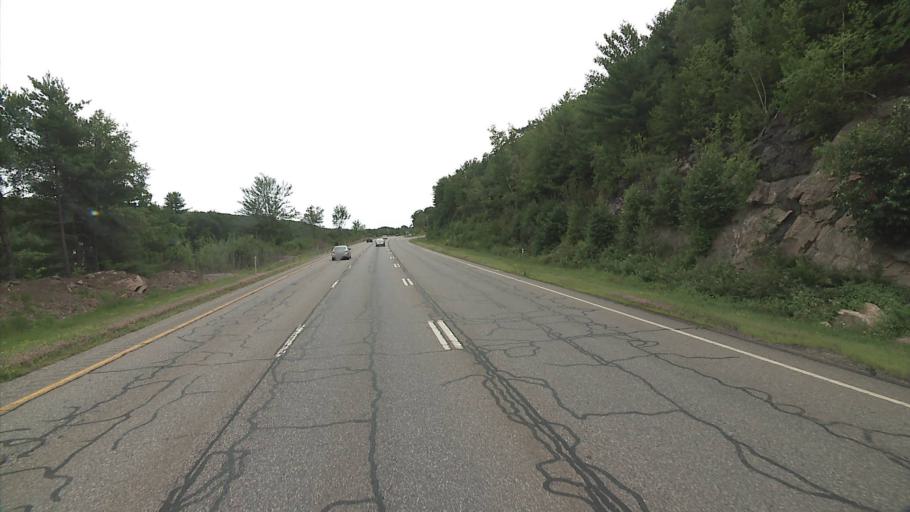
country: US
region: Connecticut
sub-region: Litchfield County
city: Torrington
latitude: 41.8262
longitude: -73.1082
